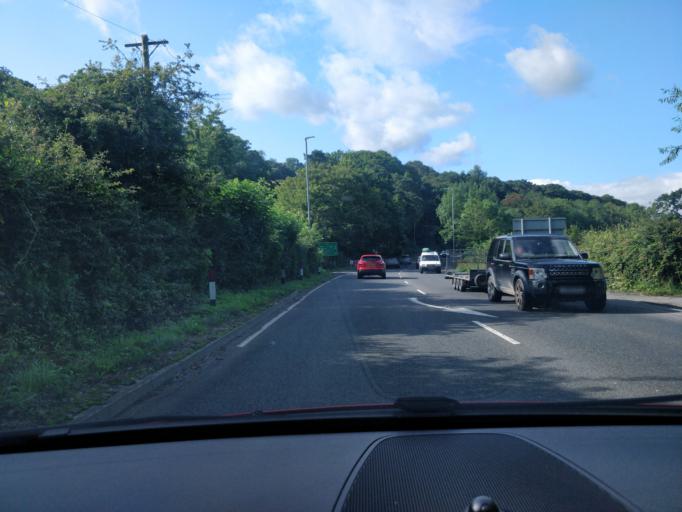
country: GB
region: Wales
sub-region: Conwy
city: Llansantffraid Glan Conwy
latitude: 53.2778
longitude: -3.7916
